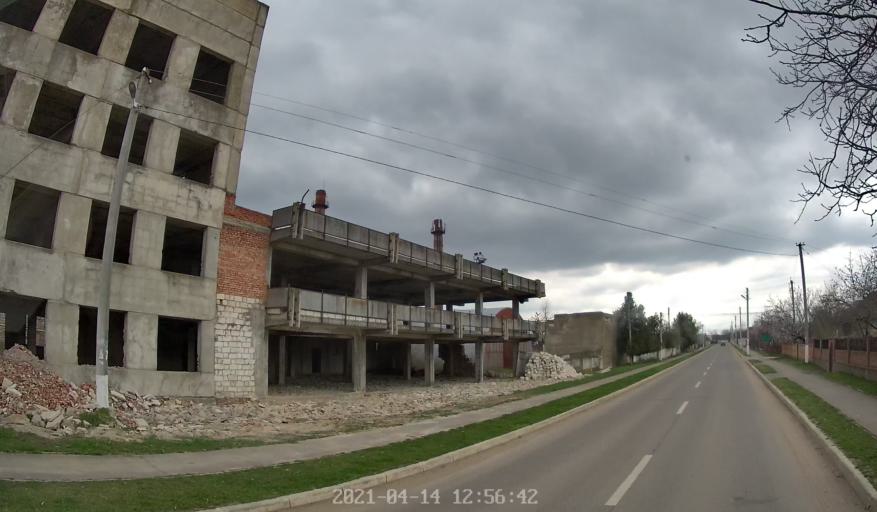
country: MD
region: Criuleni
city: Criuleni
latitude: 47.1536
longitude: 29.1465
